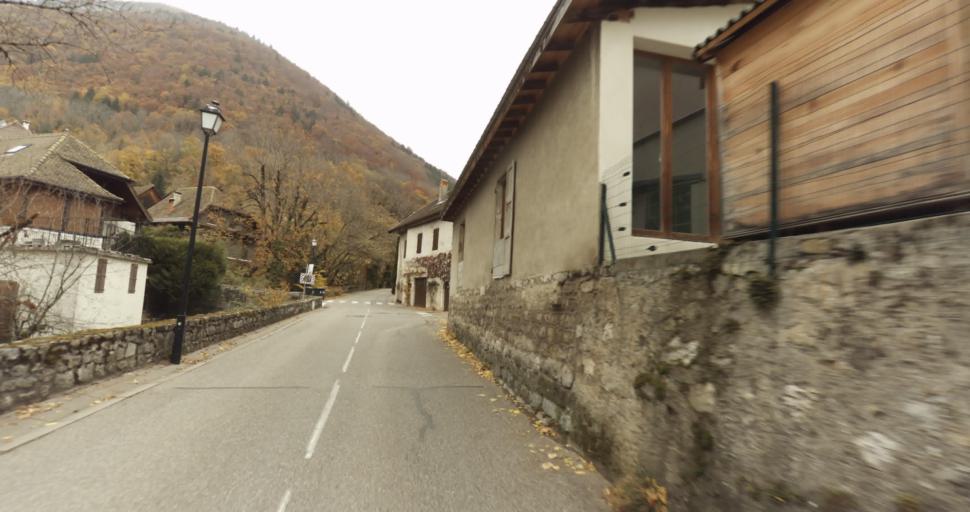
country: FR
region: Rhone-Alpes
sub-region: Departement de la Haute-Savoie
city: Menthon-Saint-Bernard
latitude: 45.8631
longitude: 6.1998
